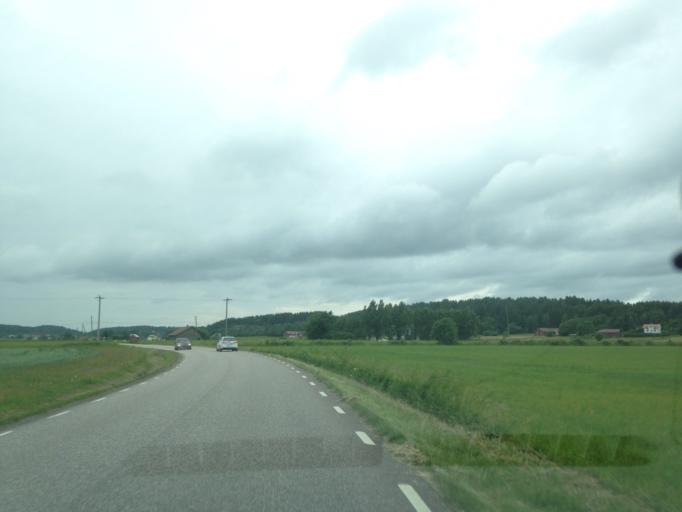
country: SE
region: Vaestra Goetaland
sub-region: Kungalvs Kommun
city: Kode
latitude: 57.8283
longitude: 11.8148
